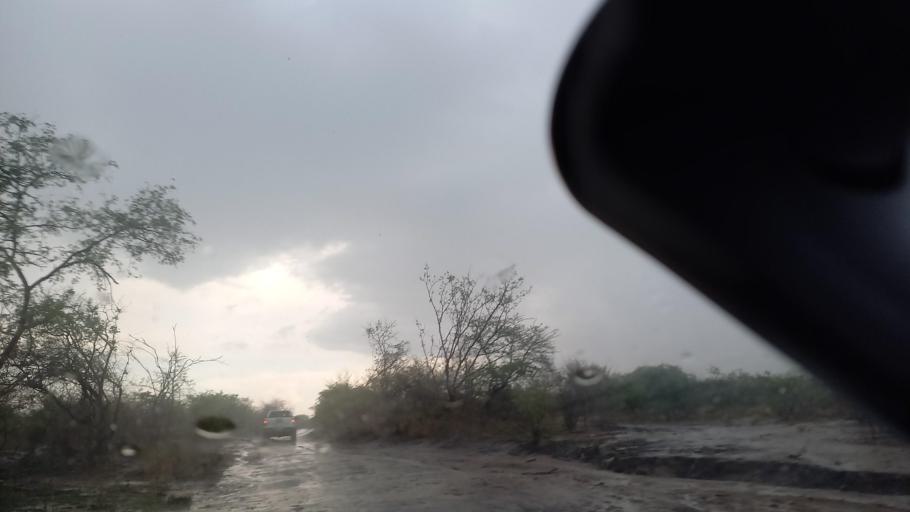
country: ZM
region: Lusaka
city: Kafue
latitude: -15.9414
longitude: 28.2152
